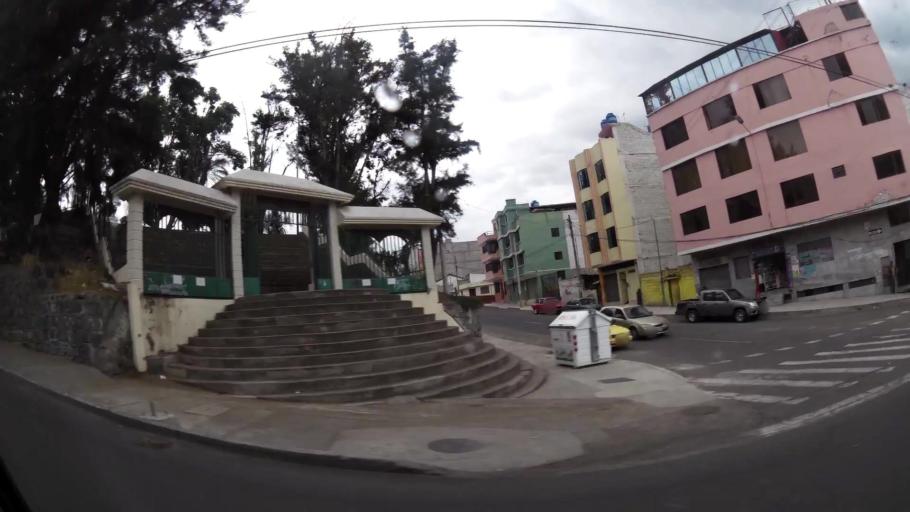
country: EC
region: Tungurahua
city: Ambato
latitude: -1.2340
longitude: -78.6231
